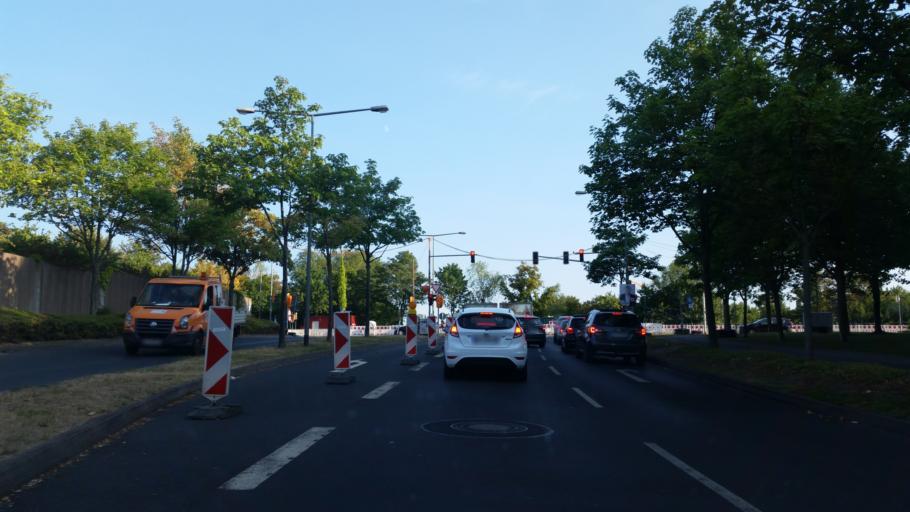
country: DE
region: Hesse
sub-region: Regierungsbezirk Kassel
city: Kassel
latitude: 51.3084
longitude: 9.4485
